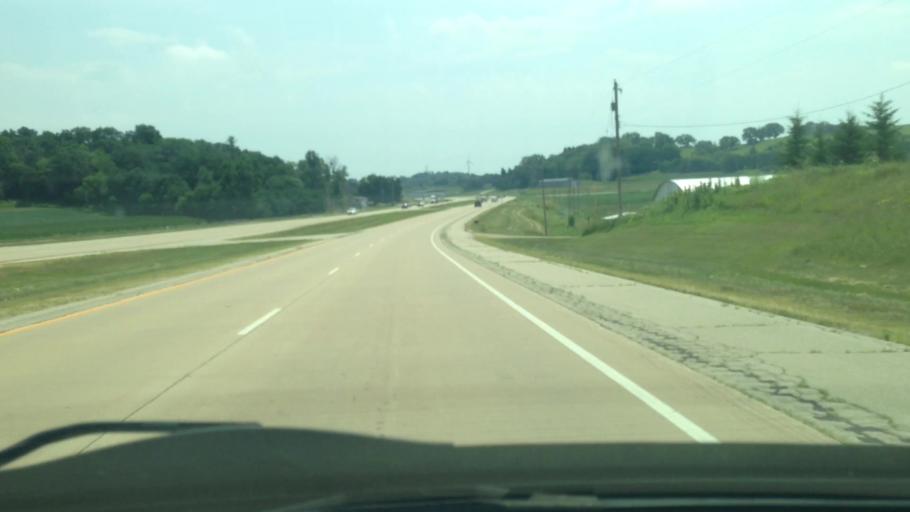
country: US
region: Wisconsin
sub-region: Dane County
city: Cross Plains
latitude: 43.1999
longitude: -89.5867
